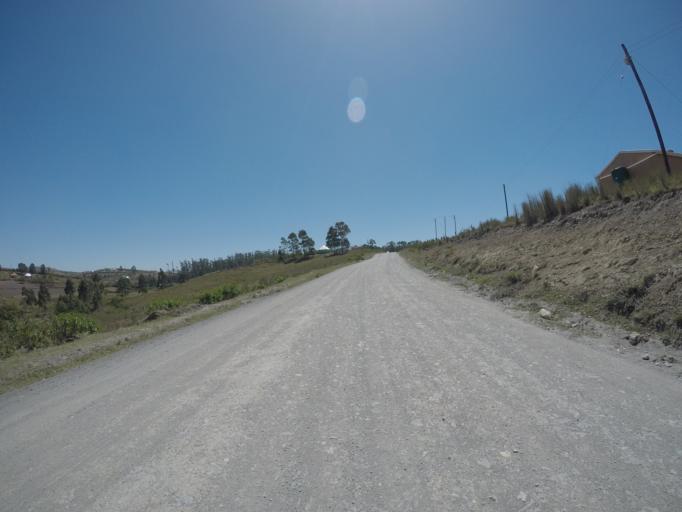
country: ZA
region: Eastern Cape
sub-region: OR Tambo District Municipality
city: Libode
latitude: -31.9653
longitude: 29.0251
